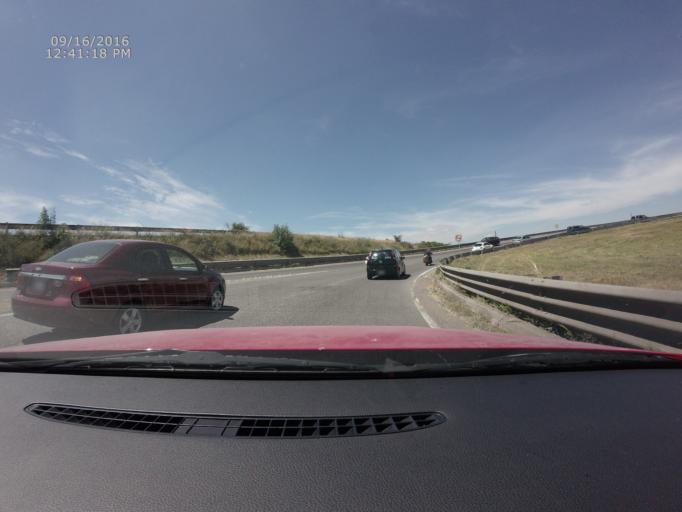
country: MX
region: Queretaro
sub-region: El Marques
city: General Lazaro Cardenas (El Colorado)
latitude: 20.5578
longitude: -100.2248
